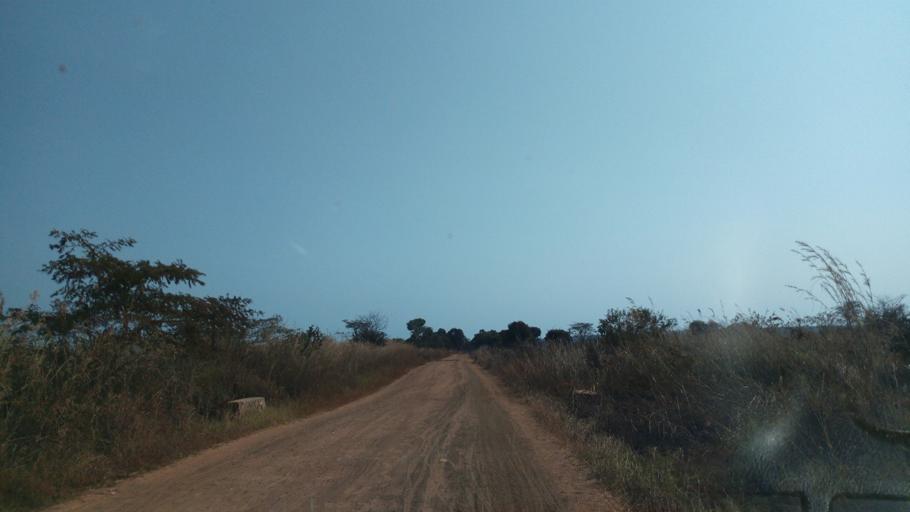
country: ZM
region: Luapula
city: Nchelenge
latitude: -9.1233
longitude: 28.3034
